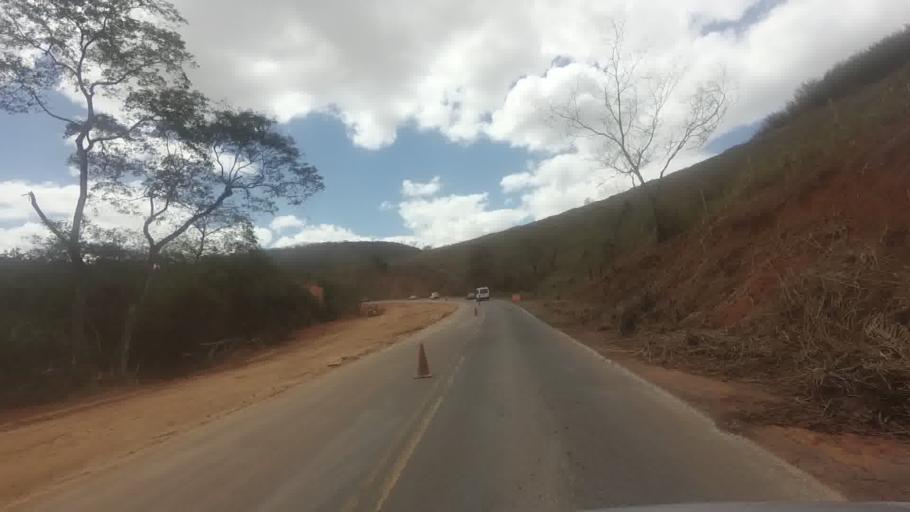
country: BR
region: Rio de Janeiro
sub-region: Santo Antonio De Padua
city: Santo Antonio de Padua
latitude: -21.5177
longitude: -42.1025
